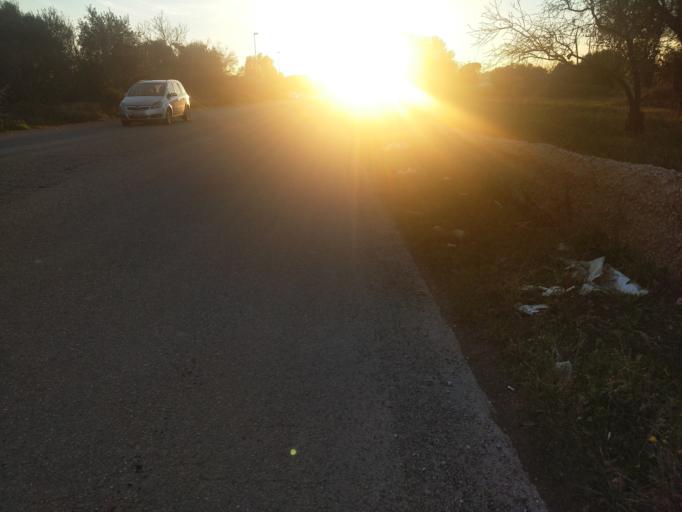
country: IT
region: Apulia
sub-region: Provincia di Bari
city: Modugno
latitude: 41.0854
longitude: 16.8015
